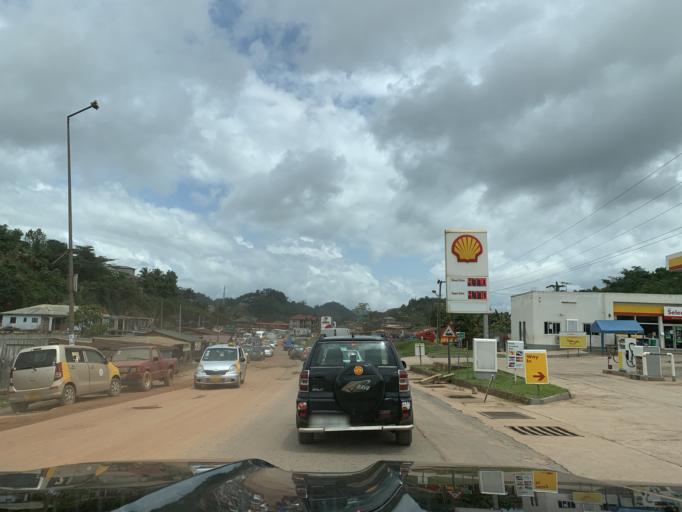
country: GH
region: Western
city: Tarkwa
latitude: 5.3297
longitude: -1.9802
